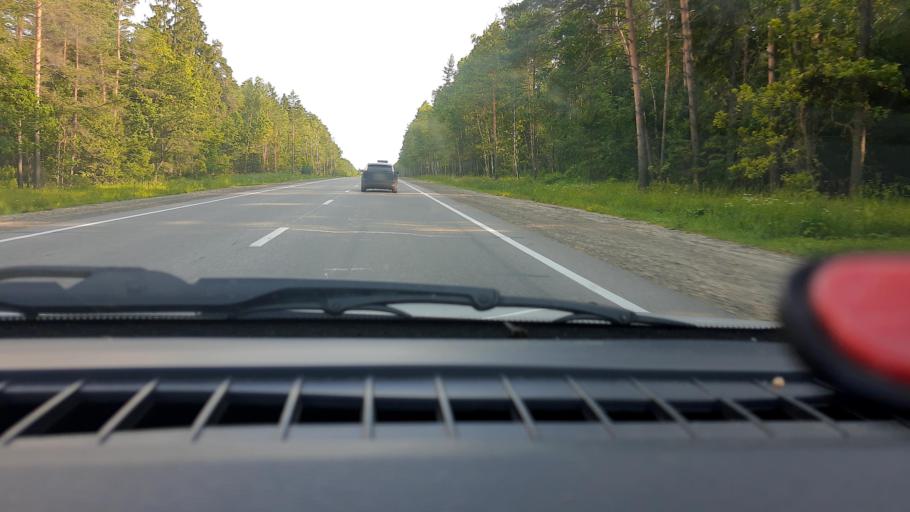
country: RU
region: Nizjnij Novgorod
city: Surovatikha
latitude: 55.7247
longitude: 43.9887
